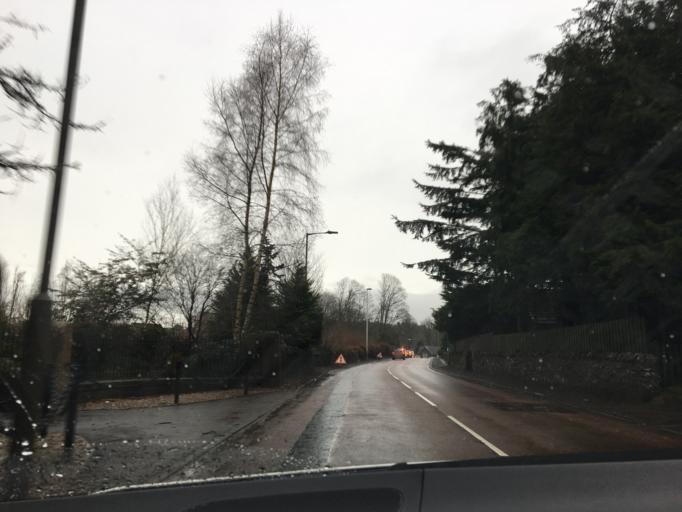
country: GB
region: Scotland
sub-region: Stirling
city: Doune
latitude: 56.1880
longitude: -4.0575
